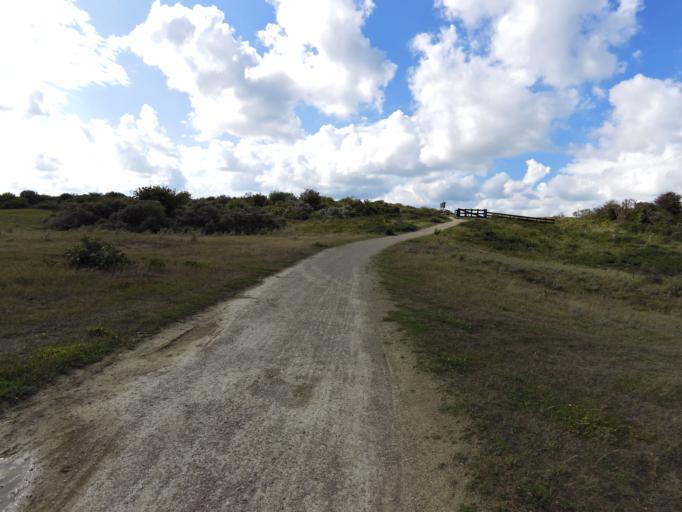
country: NL
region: South Holland
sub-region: Gemeente Goeree-Overflakkee
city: Ouddorp
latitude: 51.8344
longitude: 3.9542
